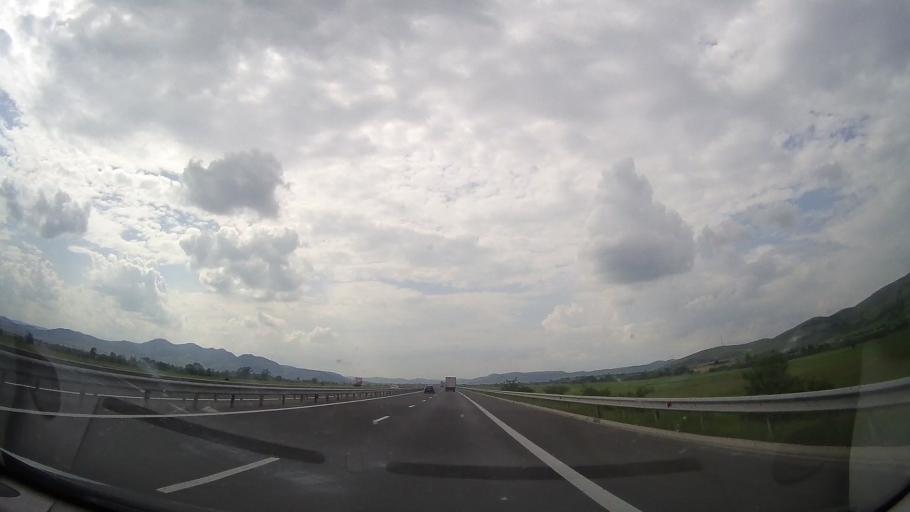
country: RO
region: Hunedoara
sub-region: Comuna Harau
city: Harau
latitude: 45.8859
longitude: 22.9824
